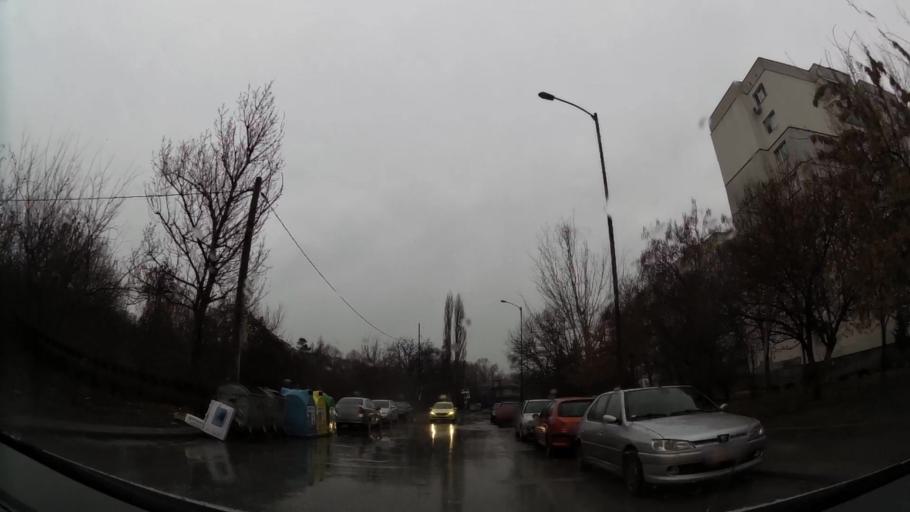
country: BG
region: Sofia-Capital
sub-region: Stolichna Obshtina
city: Sofia
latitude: 42.6549
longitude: 23.3649
